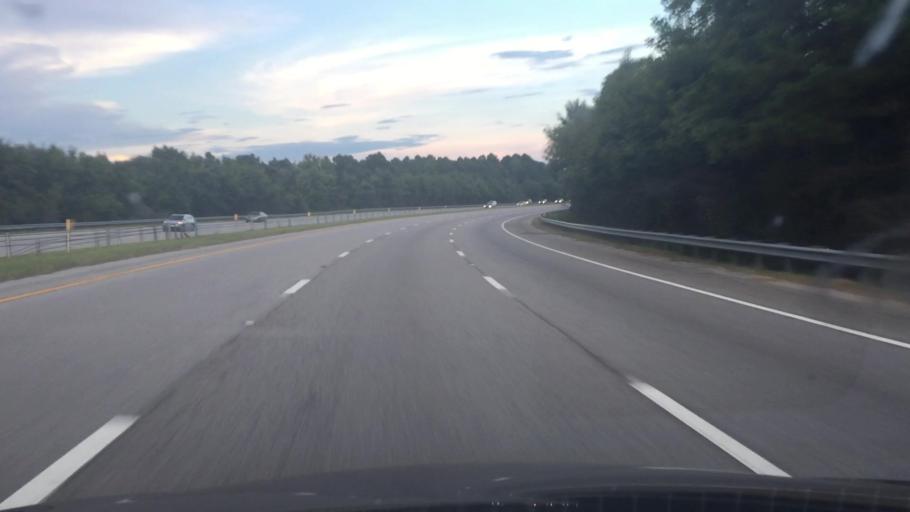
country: US
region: South Carolina
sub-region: Horry County
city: North Myrtle Beach
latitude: 33.8247
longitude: -78.7332
